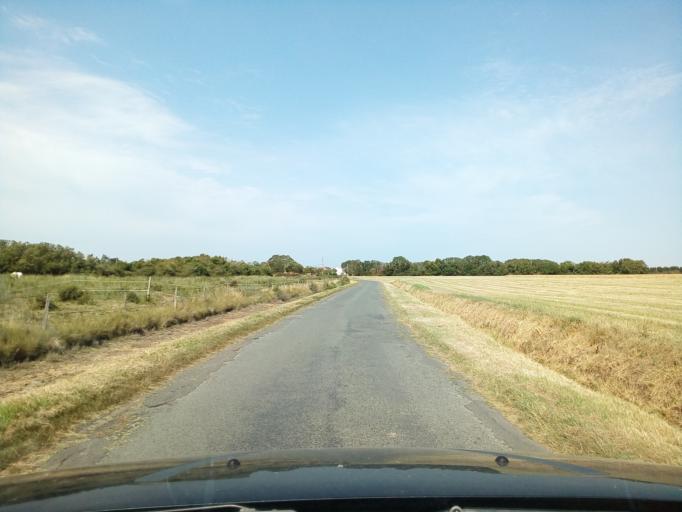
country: FR
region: Poitou-Charentes
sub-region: Departement de la Charente-Maritime
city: Dolus-d'Oleron
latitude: 45.9473
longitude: -1.2919
